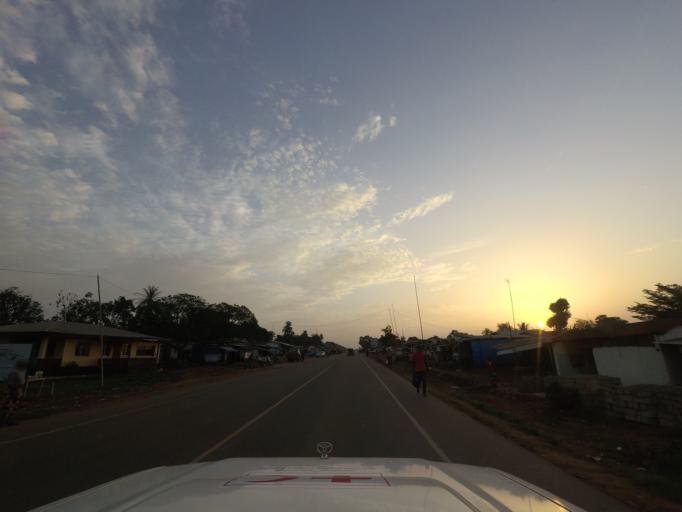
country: LR
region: Montserrado
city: Bensonville City
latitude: 6.3488
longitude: -10.6543
